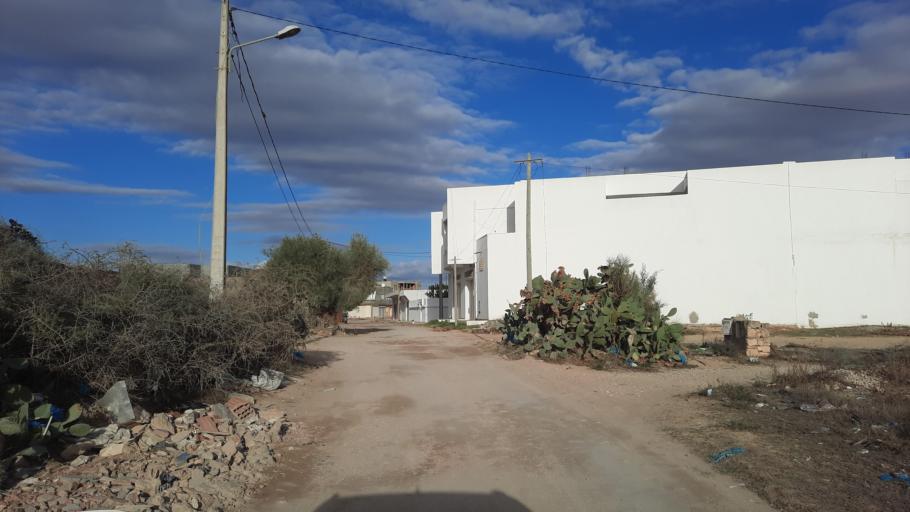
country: TN
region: Al Mahdiyah
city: El Jem
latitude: 35.2880
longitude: 10.7023
